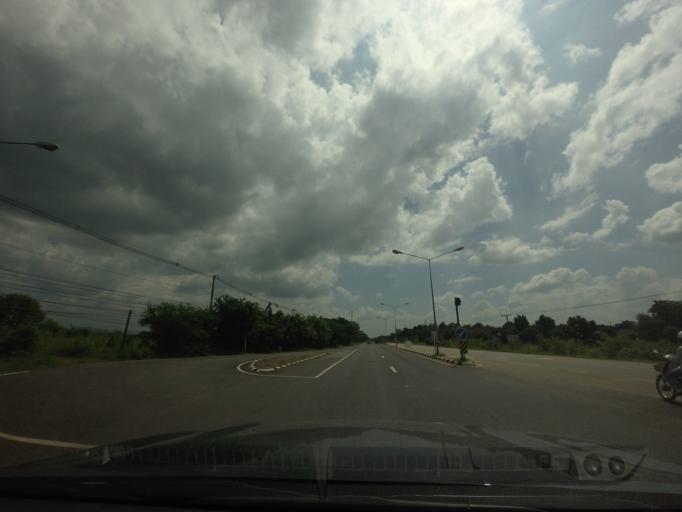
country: TH
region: Phetchabun
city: Nong Phai
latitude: 16.1988
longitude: 101.0890
